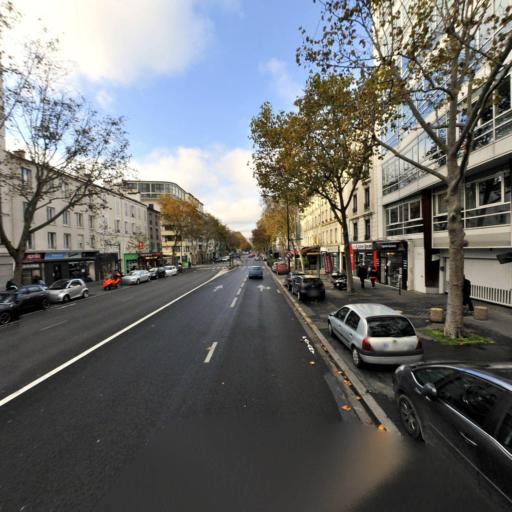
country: FR
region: Ile-de-France
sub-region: Departement des Hauts-de-Seine
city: Boulogne-Billancourt
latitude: 48.8399
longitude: 2.2384
